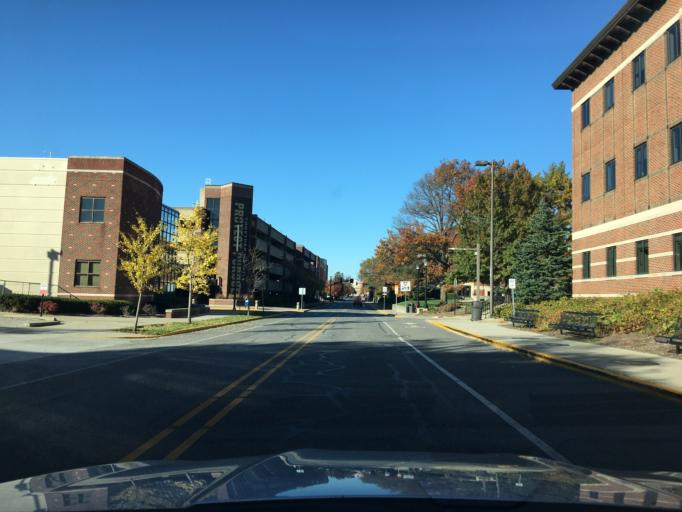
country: US
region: Indiana
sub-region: Tippecanoe County
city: West Lafayette
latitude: 40.4256
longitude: -86.9166
